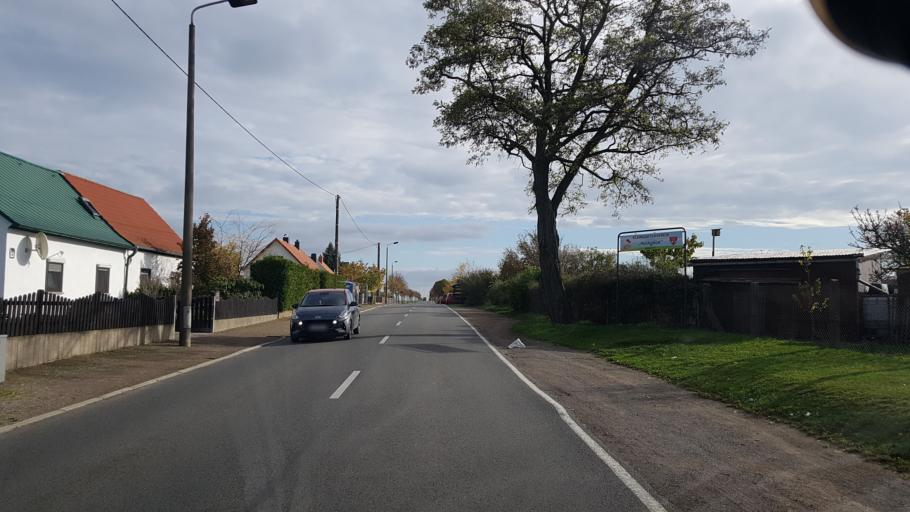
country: DE
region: Saxony
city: Dahlen
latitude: 51.3620
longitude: 13.0025
